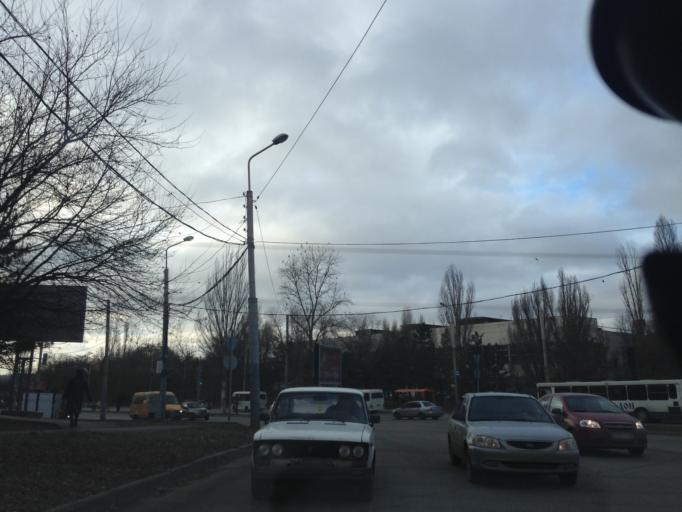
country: RU
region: Rostov
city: Severnyy
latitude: 47.2949
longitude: 39.7020
